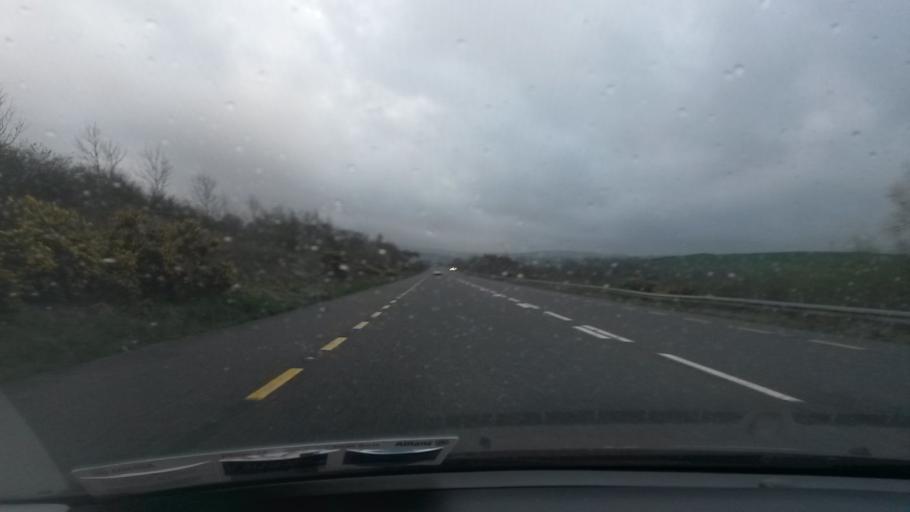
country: IE
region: Munster
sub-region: County Limerick
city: Abbeyfeale
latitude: 52.3284
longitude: -9.3589
